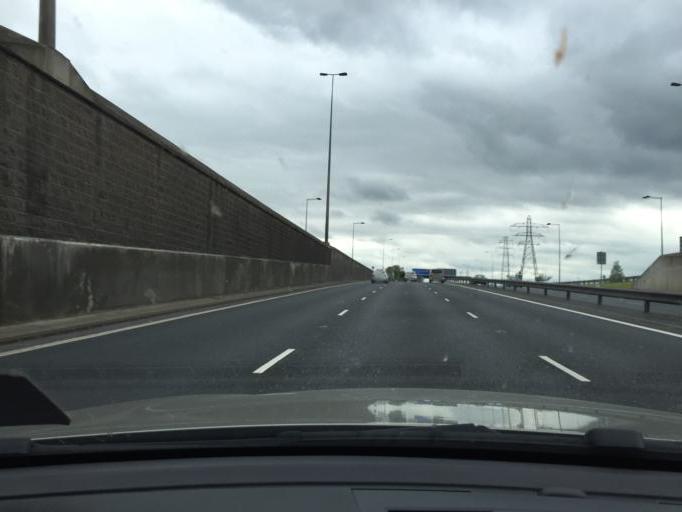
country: GB
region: Northern Ireland
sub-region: City of Belfast
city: Belfast
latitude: 54.5877
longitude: -5.9596
